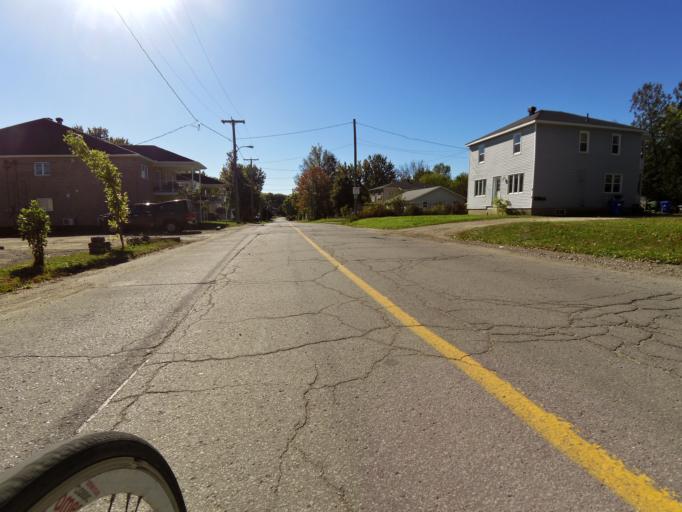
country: CA
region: Quebec
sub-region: Outaouais
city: Gatineau
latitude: 45.4809
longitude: -75.6097
